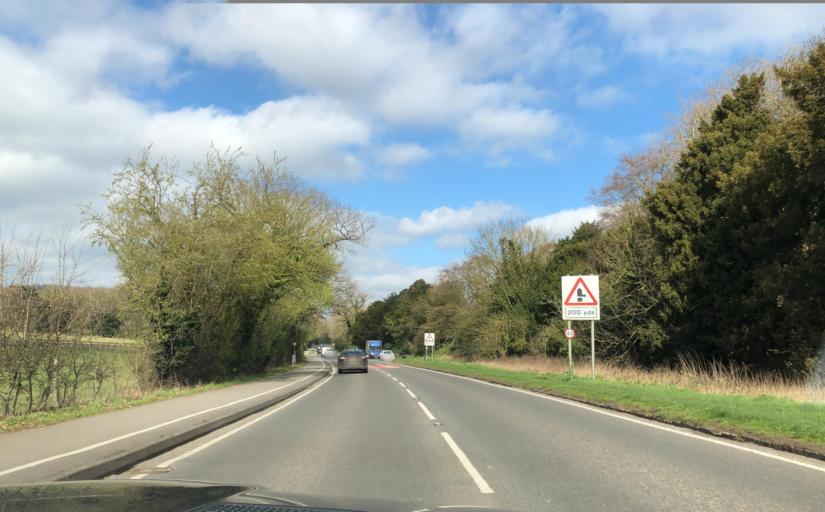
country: GB
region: England
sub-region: Warwickshire
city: Warwick
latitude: 52.2987
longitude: -1.5757
